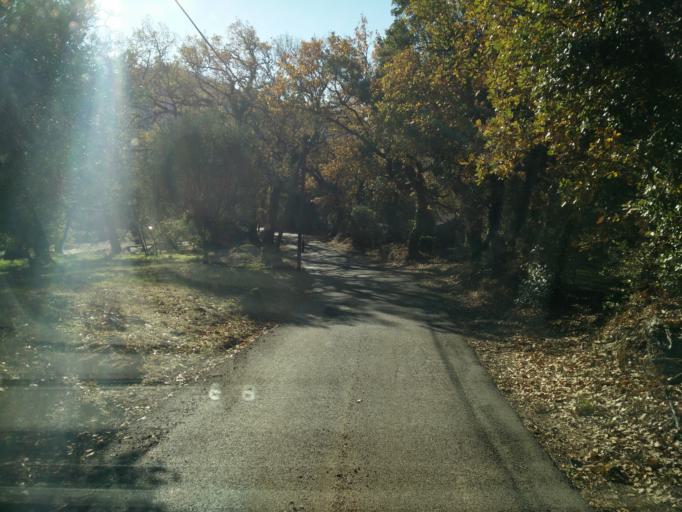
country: FR
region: Provence-Alpes-Cote d'Azur
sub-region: Departement du Var
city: La Garde-Freinet
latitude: 43.3094
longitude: 6.4790
